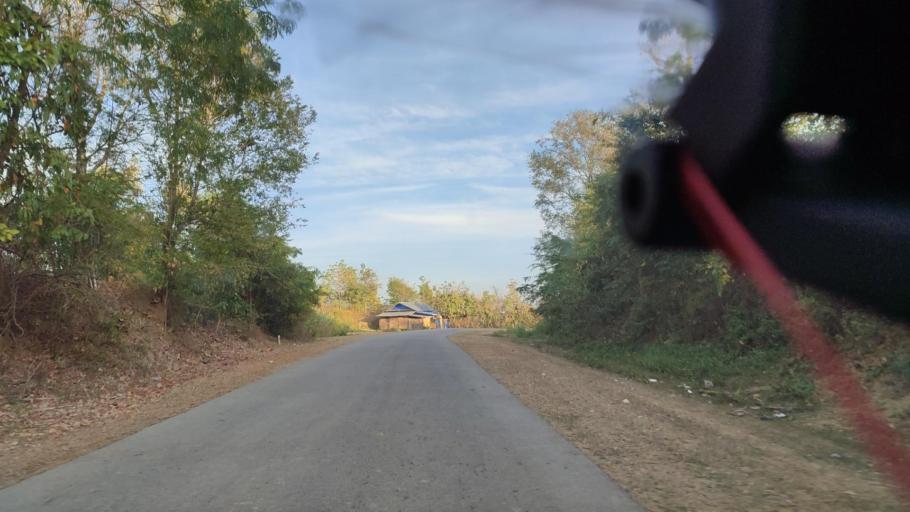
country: MM
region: Mandalay
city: Nay Pyi Taw
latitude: 19.9925
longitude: 95.9396
